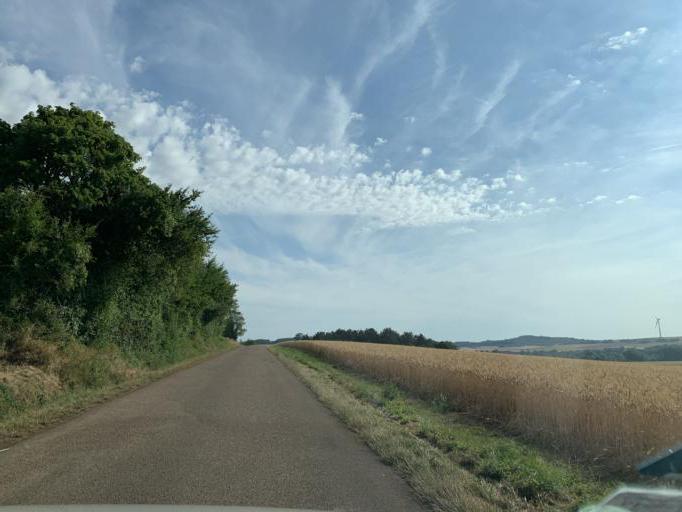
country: FR
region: Bourgogne
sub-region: Departement de la Nievre
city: Clamecy
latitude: 47.4653
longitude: 3.4268
